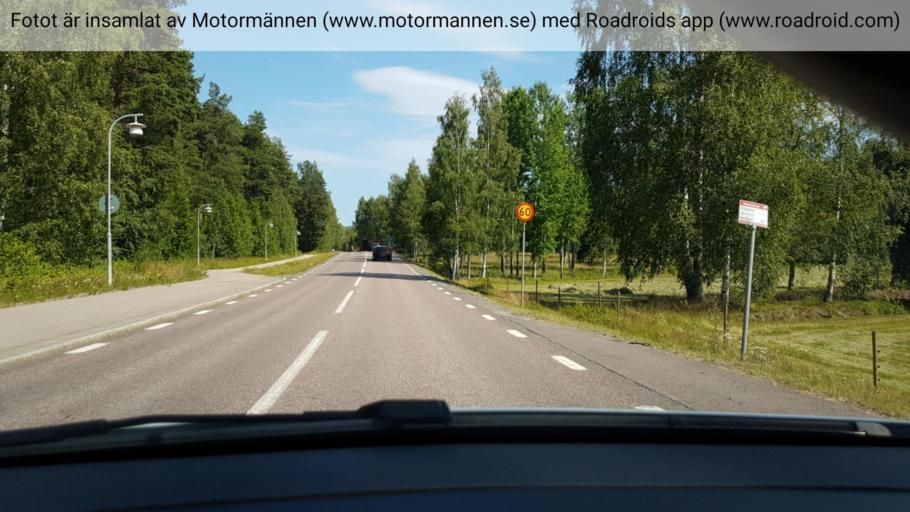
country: SE
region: Dalarna
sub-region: Faluns Kommun
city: Falun
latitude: 60.6004
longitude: 15.5791
